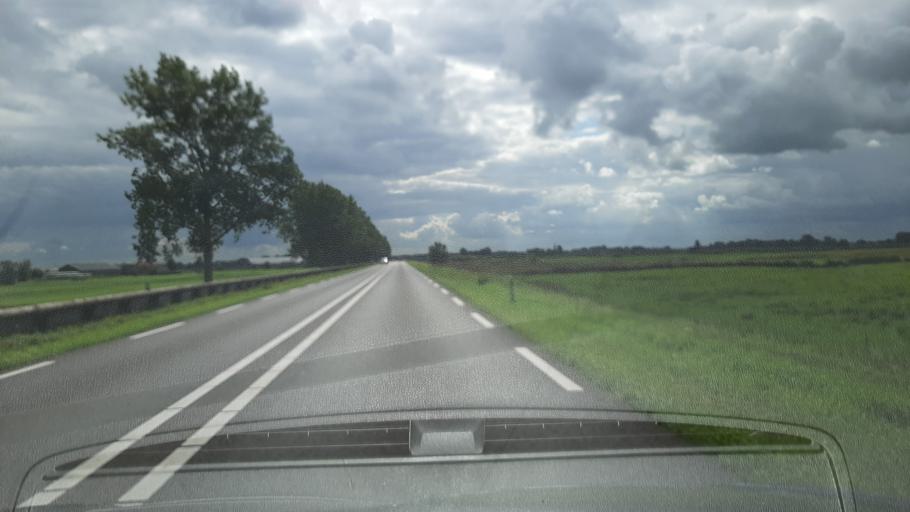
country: NL
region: Overijssel
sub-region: Gemeente Zwartewaterland
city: Hasselt
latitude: 52.6212
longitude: 6.0889
